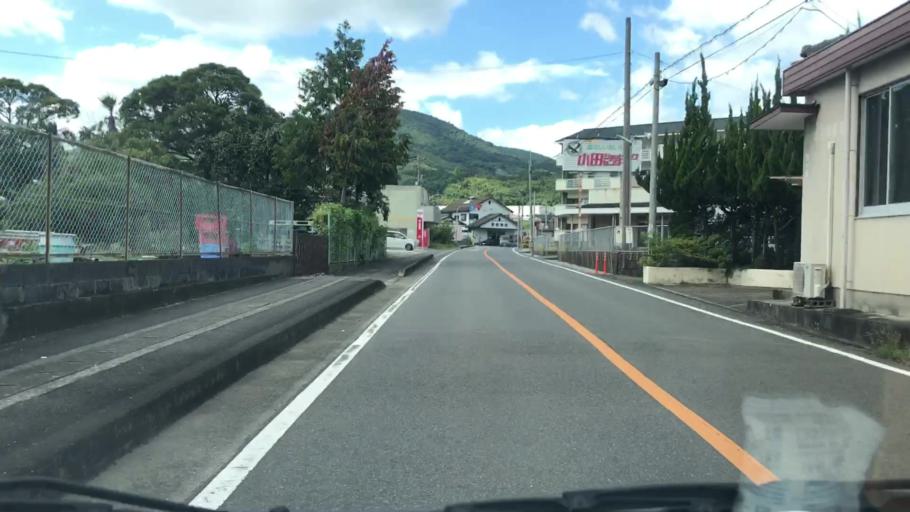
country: JP
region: Saga Prefecture
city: Takeocho-takeo
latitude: 33.2261
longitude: 130.1440
